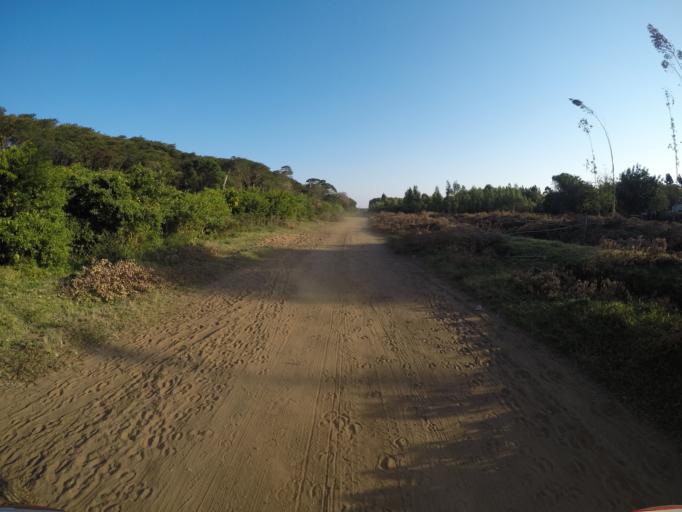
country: ZA
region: KwaZulu-Natal
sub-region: uThungulu District Municipality
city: KwaMbonambi
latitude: -28.6947
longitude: 32.1977
